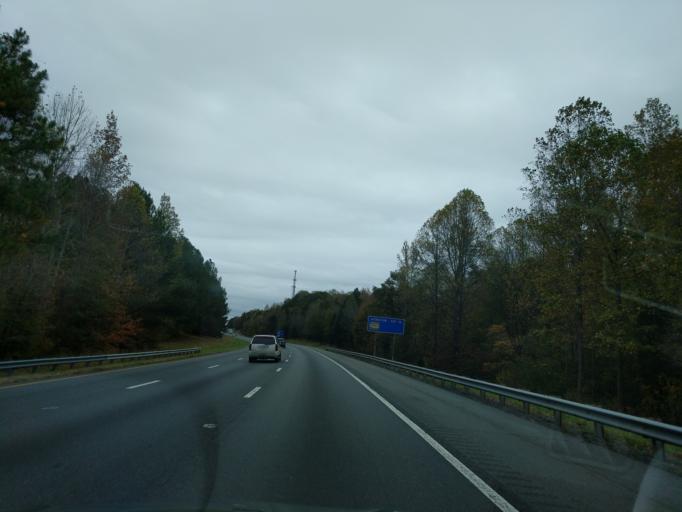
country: US
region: North Carolina
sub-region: Davidson County
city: Lexington
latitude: 35.7886
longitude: -80.2279
